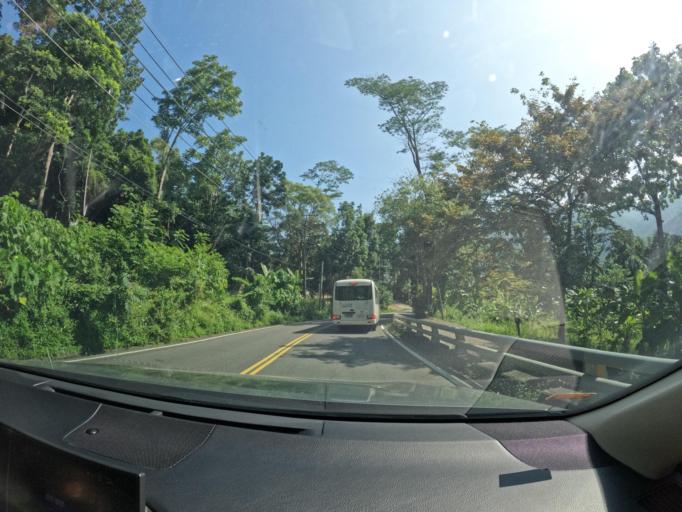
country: TW
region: Taiwan
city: Yujing
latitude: 23.0689
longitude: 120.6682
